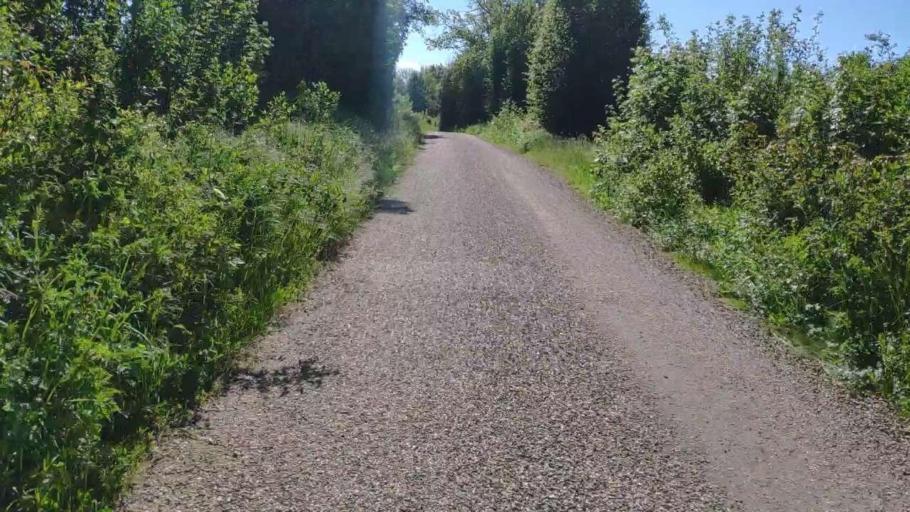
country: FR
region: Franche-Comte
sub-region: Departement du Jura
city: Perrigny
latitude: 46.6858
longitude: 5.6692
